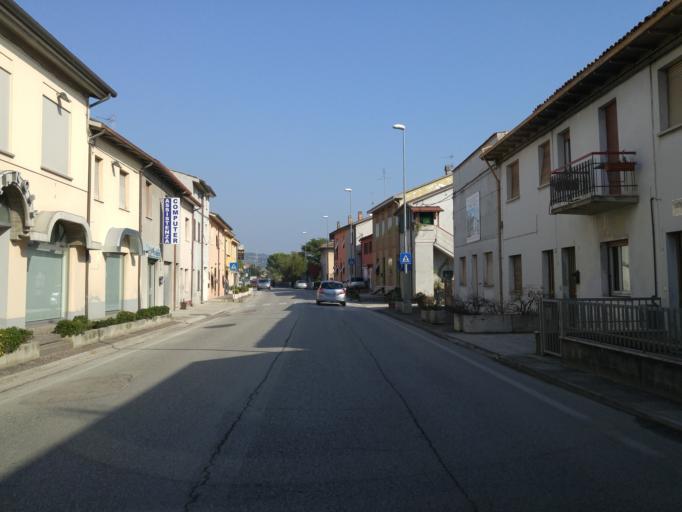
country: IT
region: The Marches
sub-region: Provincia di Pesaro e Urbino
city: Lucrezia
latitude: 43.7805
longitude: 12.9423
